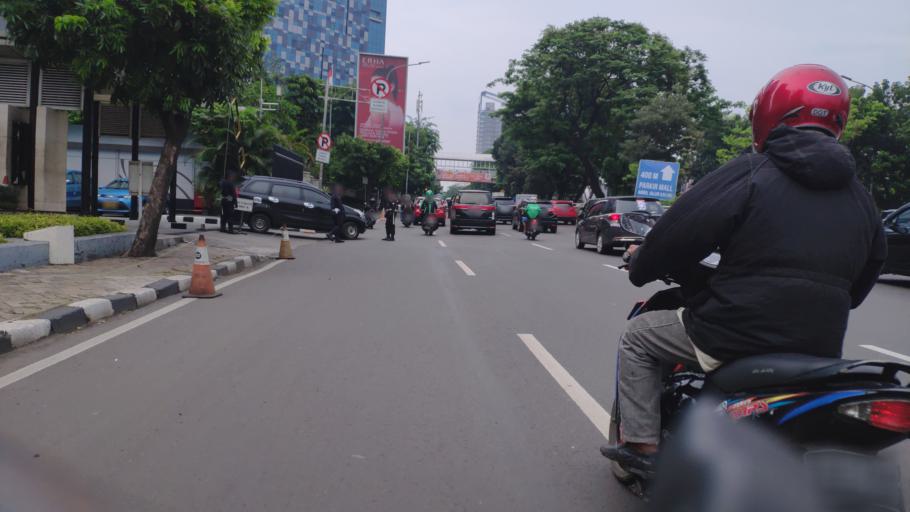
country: ID
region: Jakarta Raya
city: Jakarta
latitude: -6.2249
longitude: 106.8398
